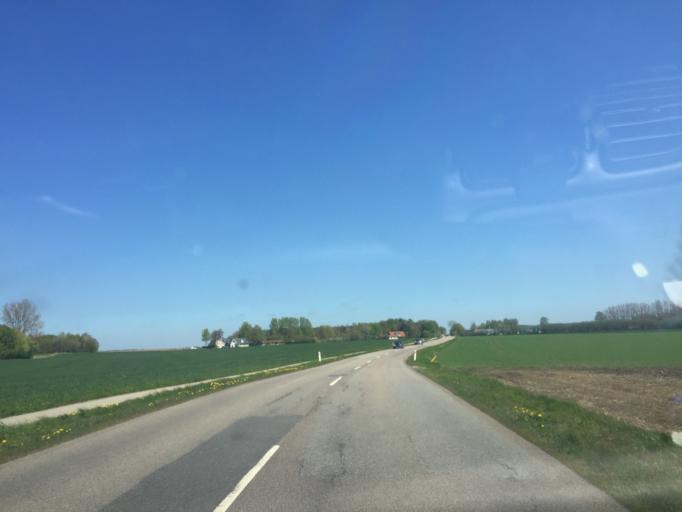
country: DK
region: Capital Region
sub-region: Egedal Kommune
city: Vekso
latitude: 55.7799
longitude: 12.2400
